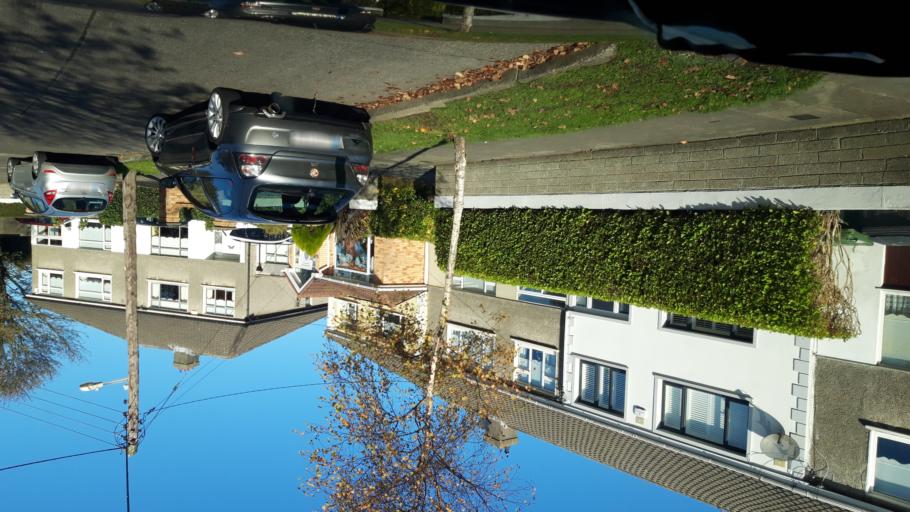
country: IE
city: Coolock
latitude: 53.3882
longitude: -6.1949
